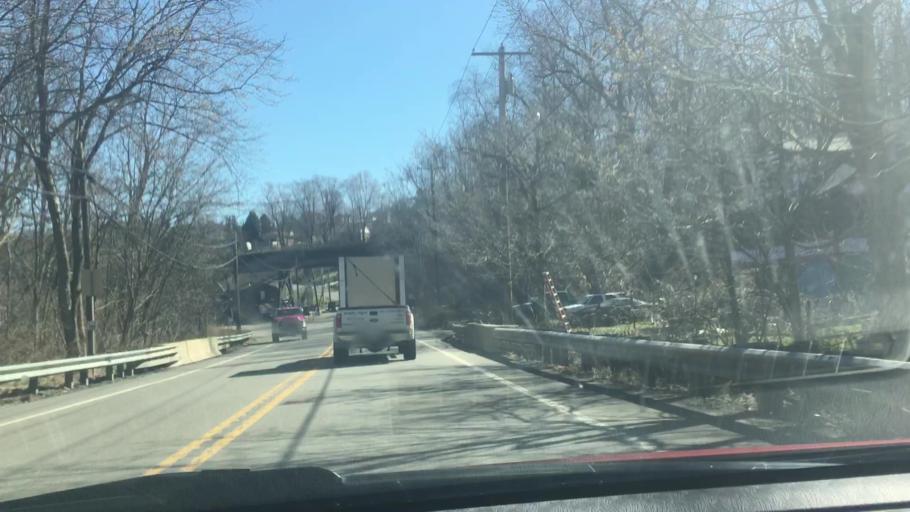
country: US
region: Pennsylvania
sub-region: Washington County
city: Baidland
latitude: 40.1949
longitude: -79.9733
